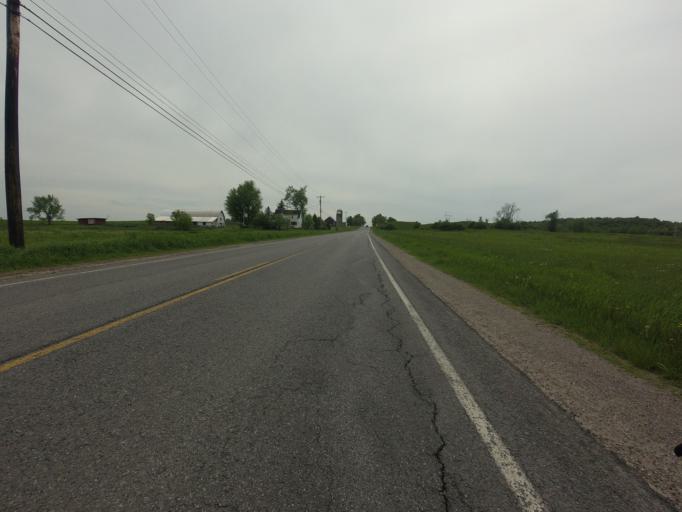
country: US
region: New York
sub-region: St. Lawrence County
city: Gouverneur
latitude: 44.3462
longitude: -75.2235
